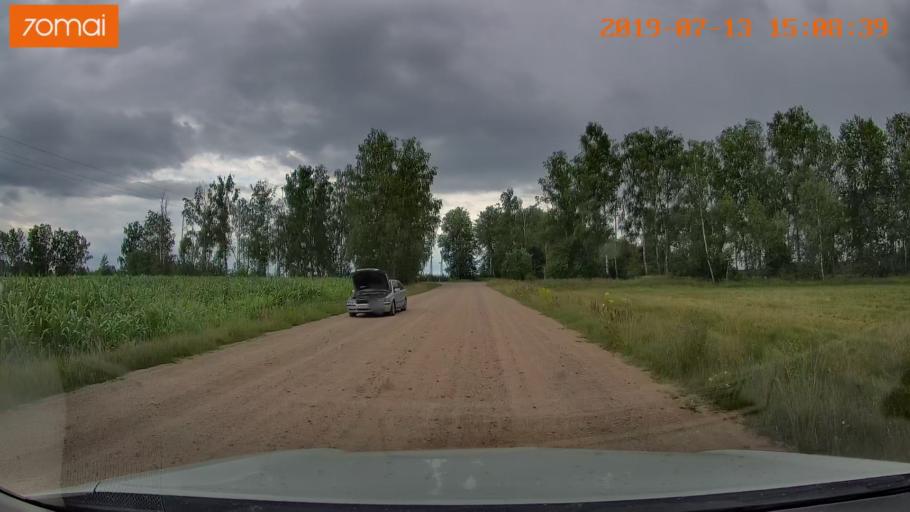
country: BY
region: Mogilev
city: Hlusha
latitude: 53.1756
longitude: 28.7549
